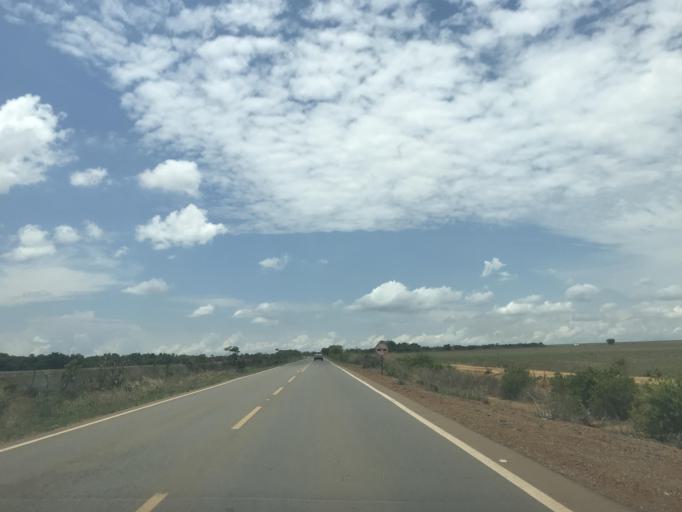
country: BR
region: Goias
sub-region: Vianopolis
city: Vianopolis
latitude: -16.5087
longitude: -48.2279
